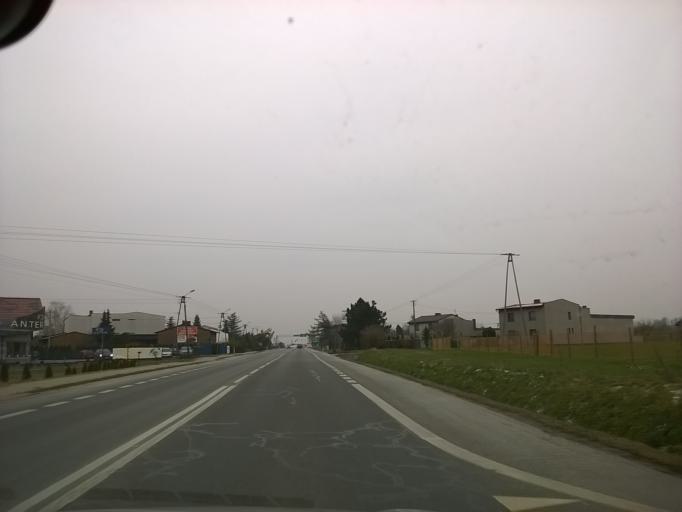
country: PL
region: Silesian Voivodeship
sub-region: Powiat gliwicki
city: Paniowki
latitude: 50.2349
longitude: 18.7841
